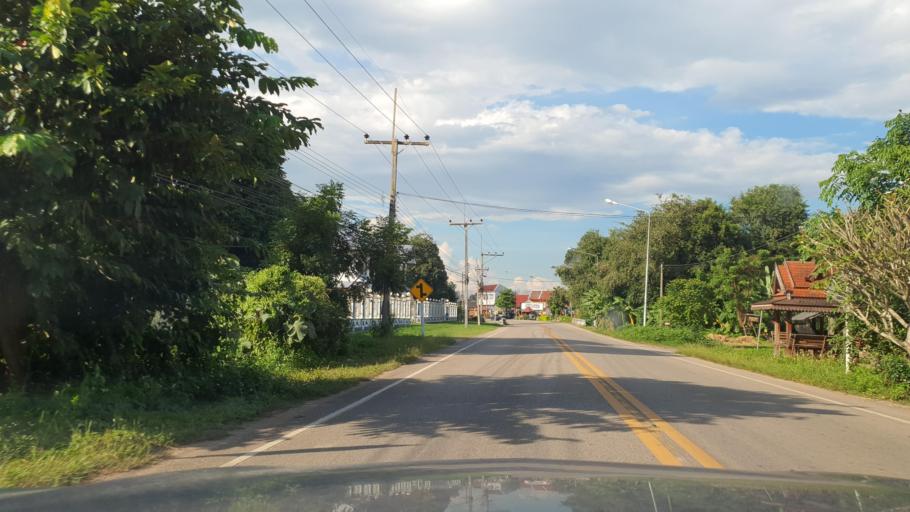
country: TH
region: Phayao
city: Phayao
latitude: 19.1460
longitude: 99.8337
